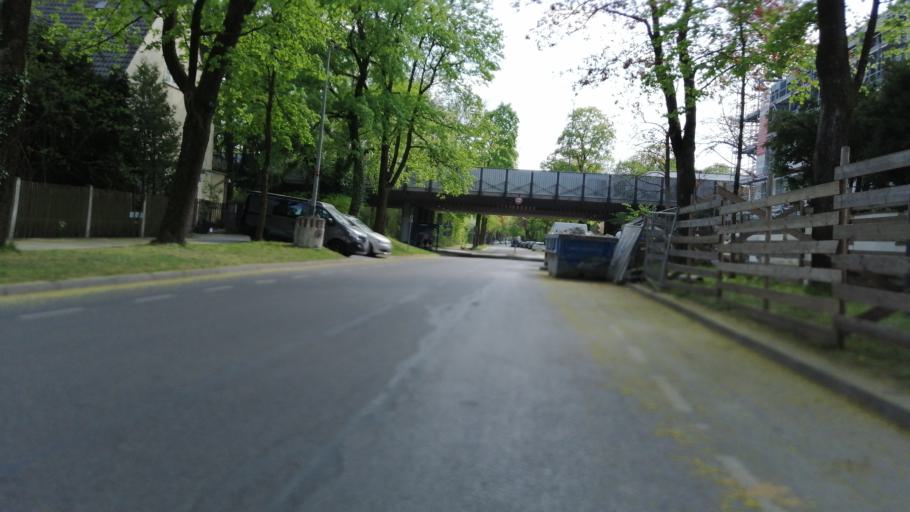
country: DE
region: Bavaria
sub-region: Upper Bavaria
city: Bogenhausen
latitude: 48.1564
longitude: 11.6094
